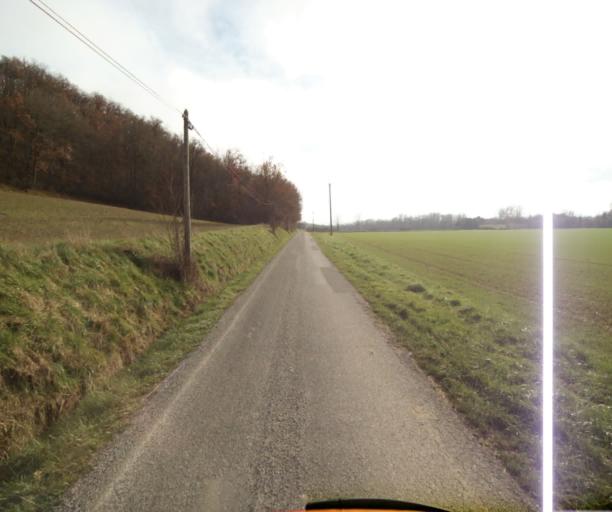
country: FR
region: Languedoc-Roussillon
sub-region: Departement de l'Aude
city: Belpech
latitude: 43.1726
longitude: 1.7380
